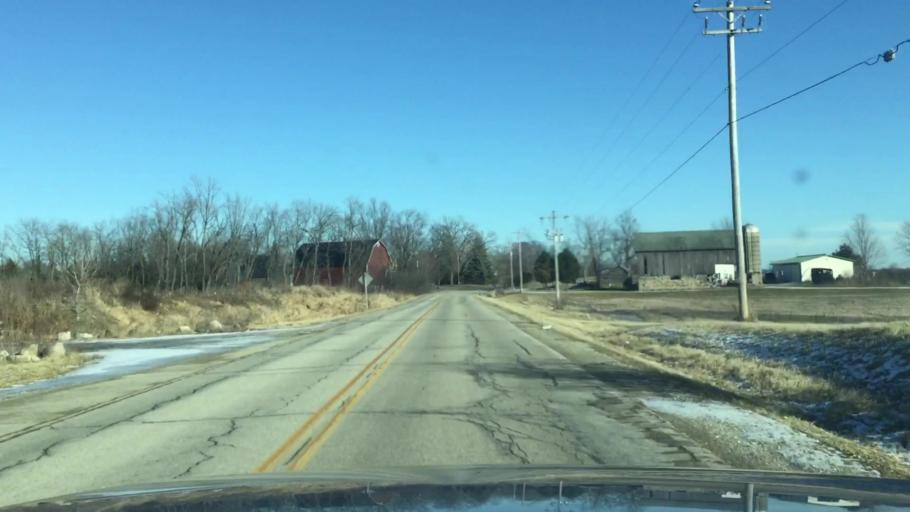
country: US
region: Wisconsin
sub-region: Racine County
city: Waterford
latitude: 42.7635
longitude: -88.1964
